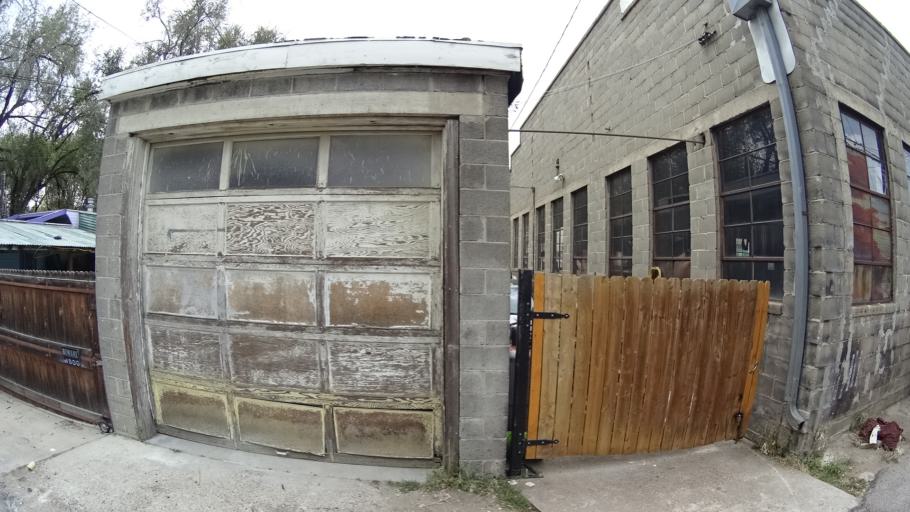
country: US
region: Colorado
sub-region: El Paso County
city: Colorado Springs
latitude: 38.8366
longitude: -104.7909
